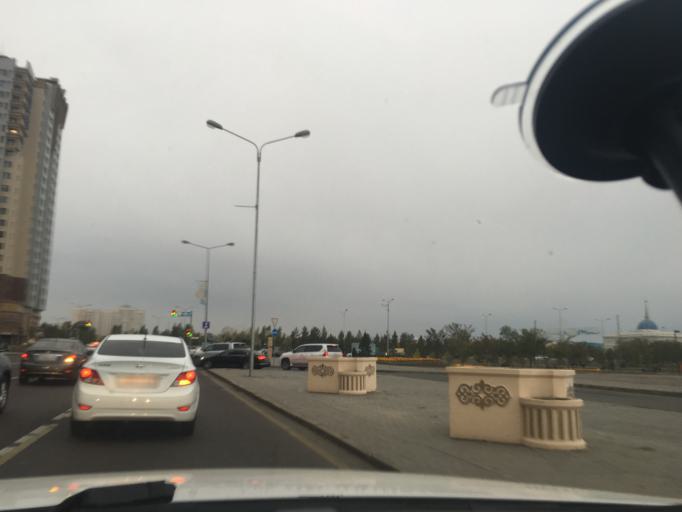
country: KZ
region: Astana Qalasy
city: Astana
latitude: 51.1306
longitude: 71.4585
